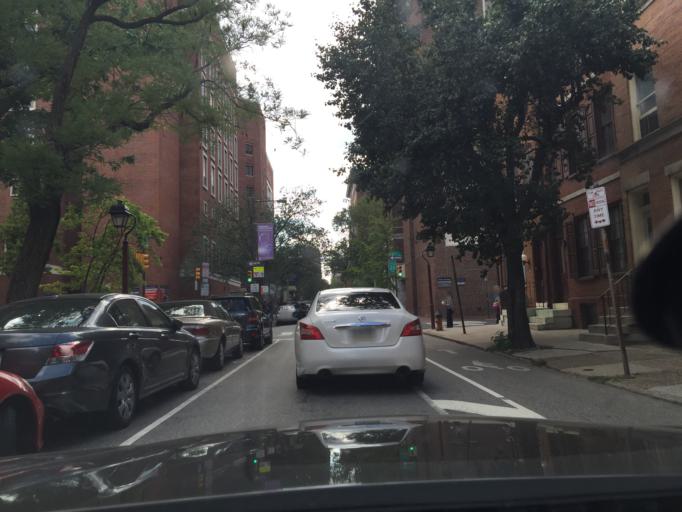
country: US
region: Pennsylvania
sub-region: Philadelphia County
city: Philadelphia
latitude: 39.9457
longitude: -75.1543
